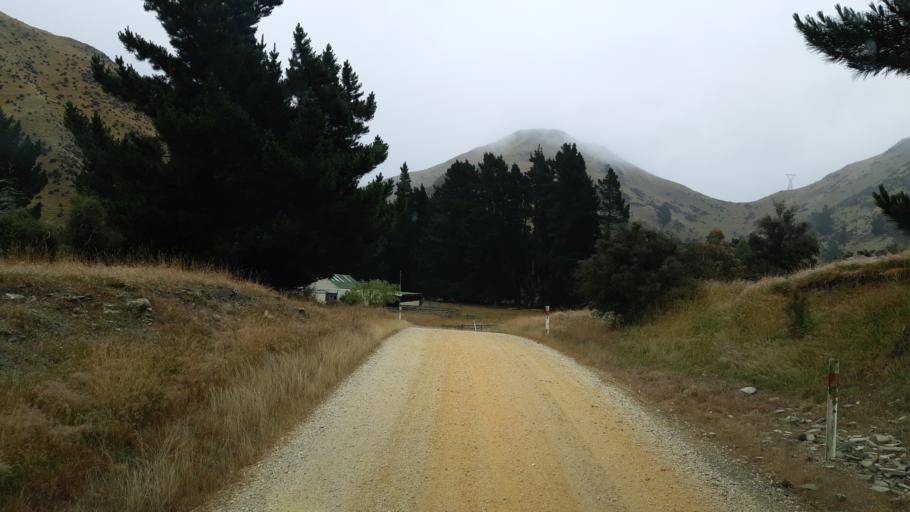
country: NZ
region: Otago
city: Oamaru
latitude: -44.9542
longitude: 170.4762
